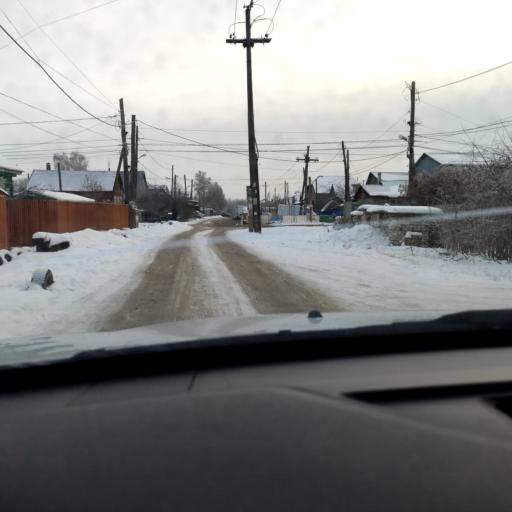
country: RU
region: Samara
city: Petra-Dubrava
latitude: 53.2523
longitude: 50.3150
